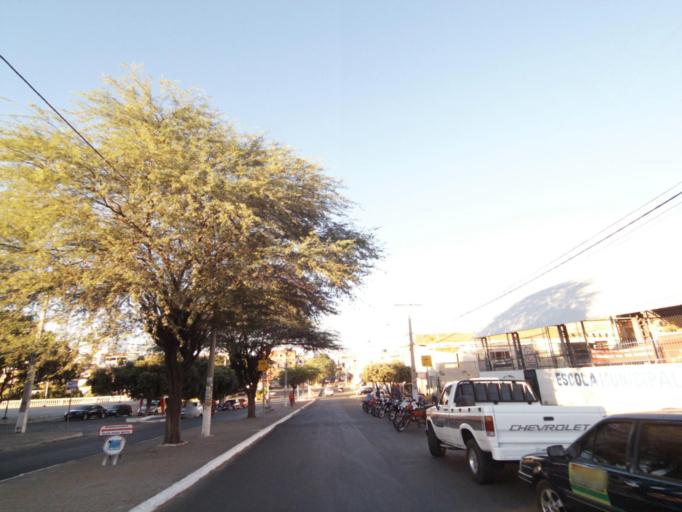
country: BR
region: Bahia
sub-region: Brumado
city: Brumado
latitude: -14.2137
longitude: -41.6771
